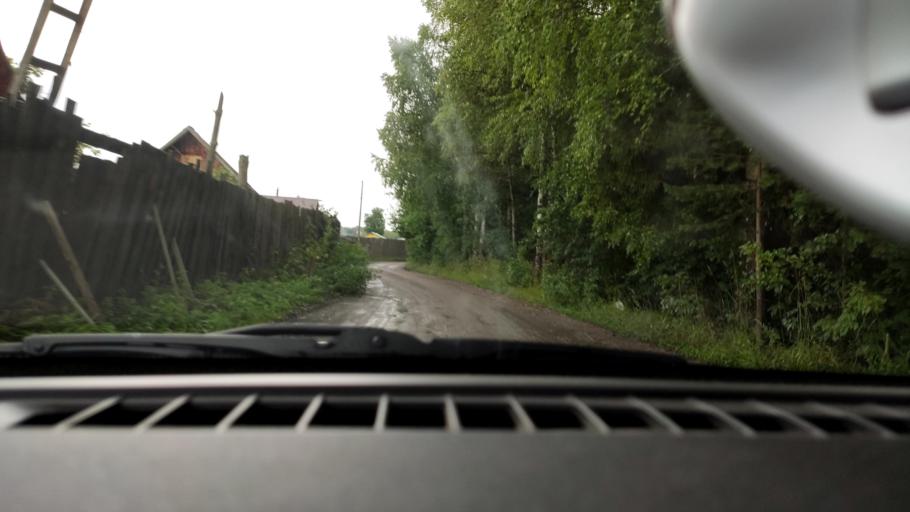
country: RU
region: Perm
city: Overyata
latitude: 58.0524
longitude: 55.9834
